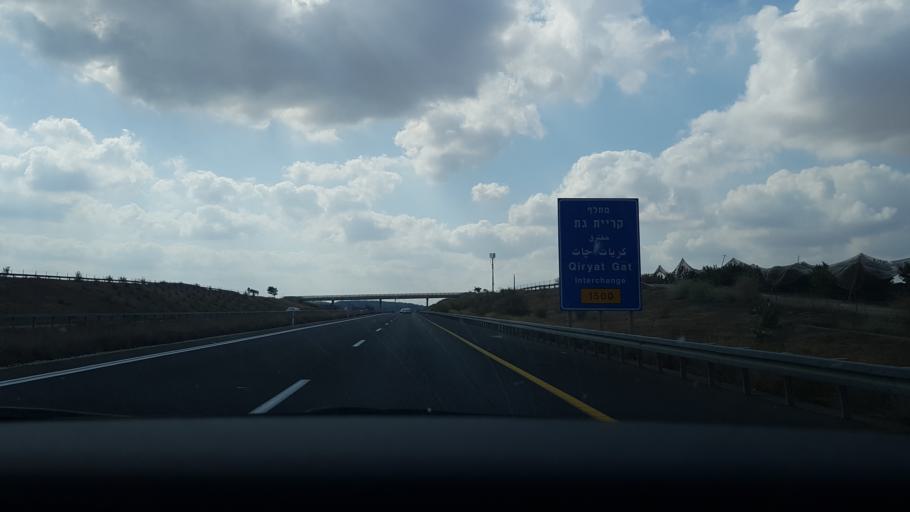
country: IL
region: Southern District
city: Qiryat Gat
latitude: 31.6183
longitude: 34.8143
